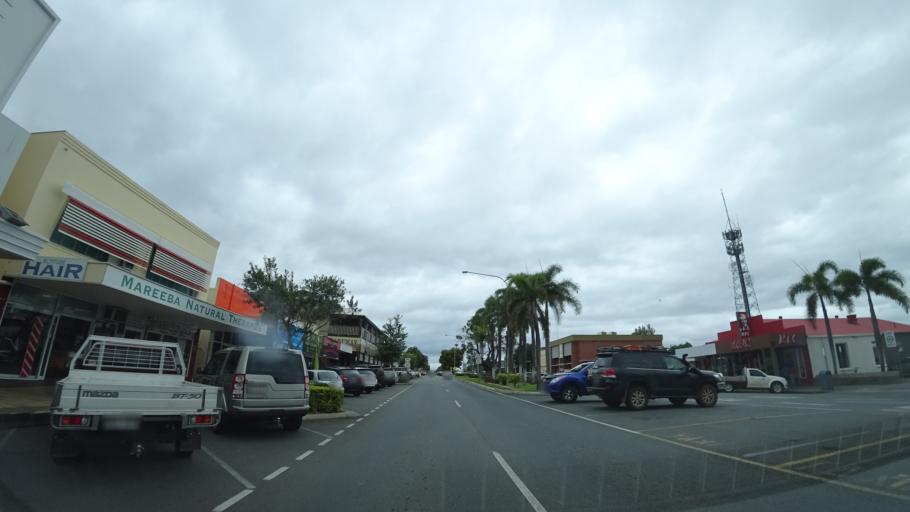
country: AU
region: Queensland
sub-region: Tablelands
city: Mareeba
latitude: -16.9920
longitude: 145.4223
